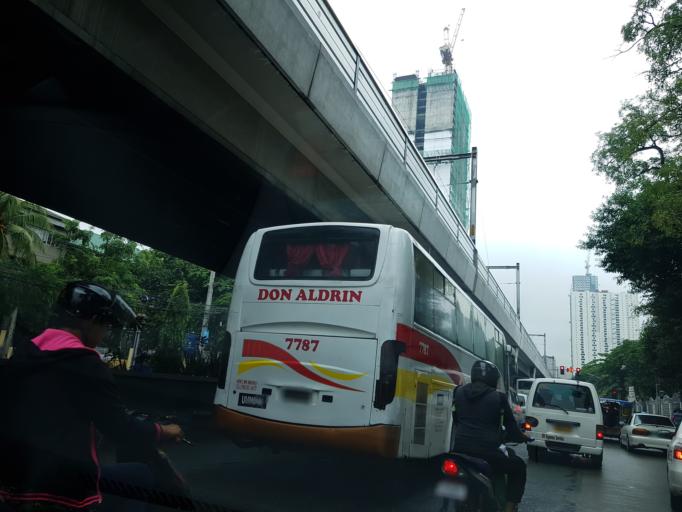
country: PH
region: Metro Manila
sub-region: City of Manila
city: Port Area
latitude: 14.5806
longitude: 120.9856
